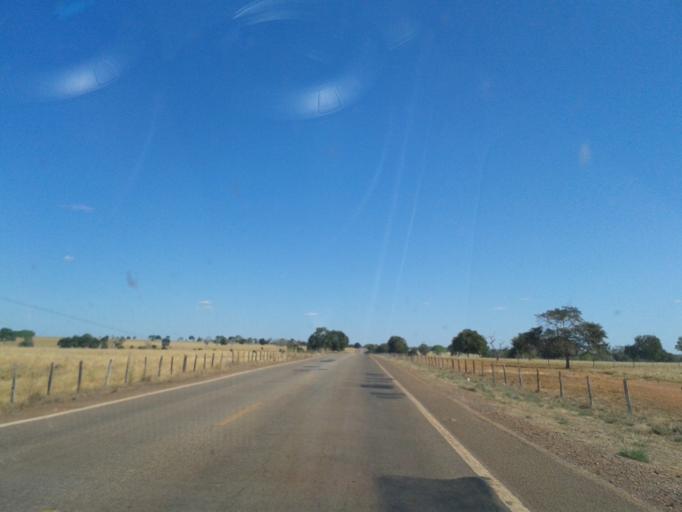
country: BR
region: Goias
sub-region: Crixas
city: Crixas
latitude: -14.1484
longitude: -50.3598
